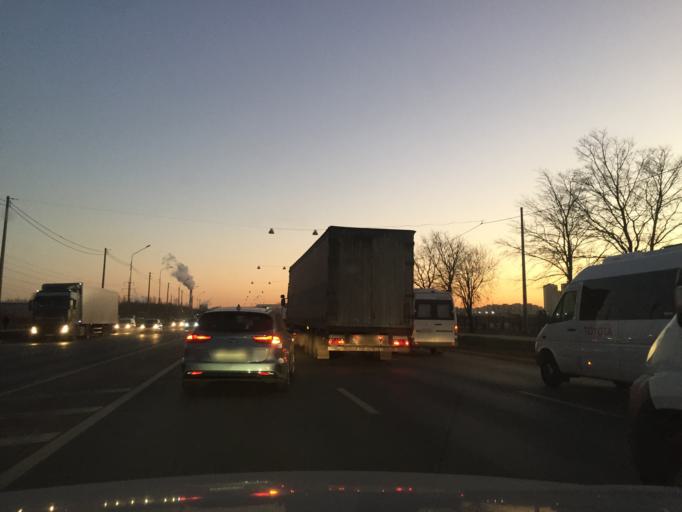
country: RU
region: St.-Petersburg
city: Obukhovo
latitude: 59.8552
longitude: 30.4242
